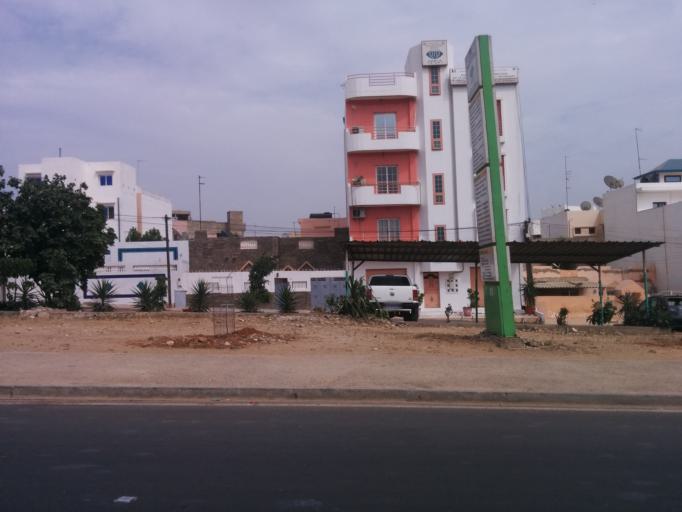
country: SN
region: Dakar
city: Mermoz Boabab
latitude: 14.7320
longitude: -17.4732
